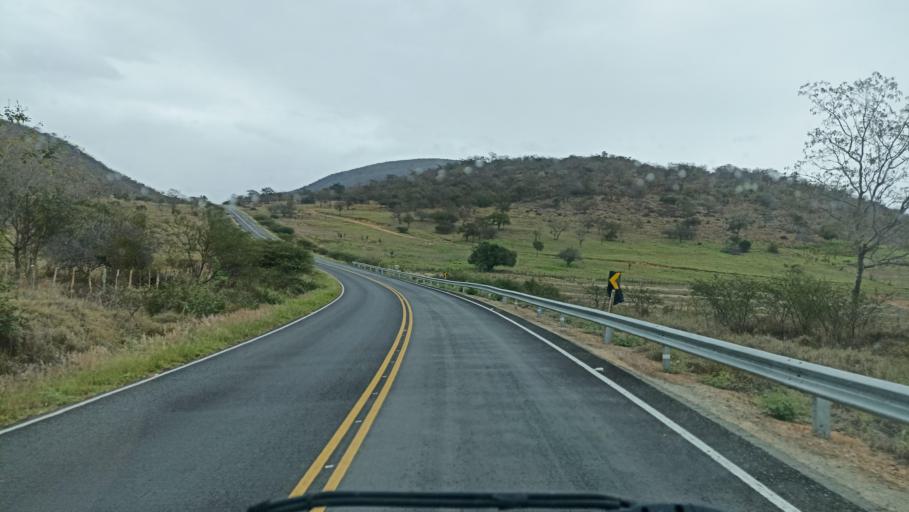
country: BR
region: Bahia
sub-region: Andarai
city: Vera Cruz
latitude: -13.0451
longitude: -40.7729
